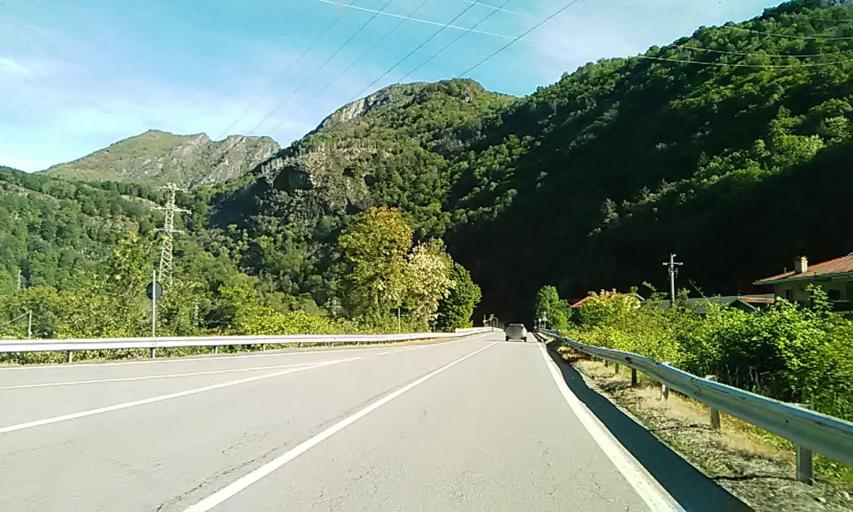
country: IT
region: Piedmont
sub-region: Provincia di Vercelli
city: Varallo
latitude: 45.8163
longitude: 8.2434
